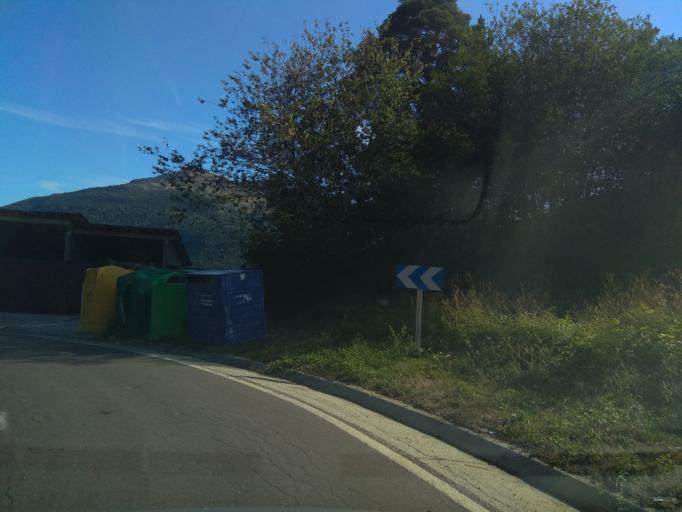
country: ES
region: Catalonia
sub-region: Provincia de Lleida
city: Les
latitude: 42.7454
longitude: 0.7301
